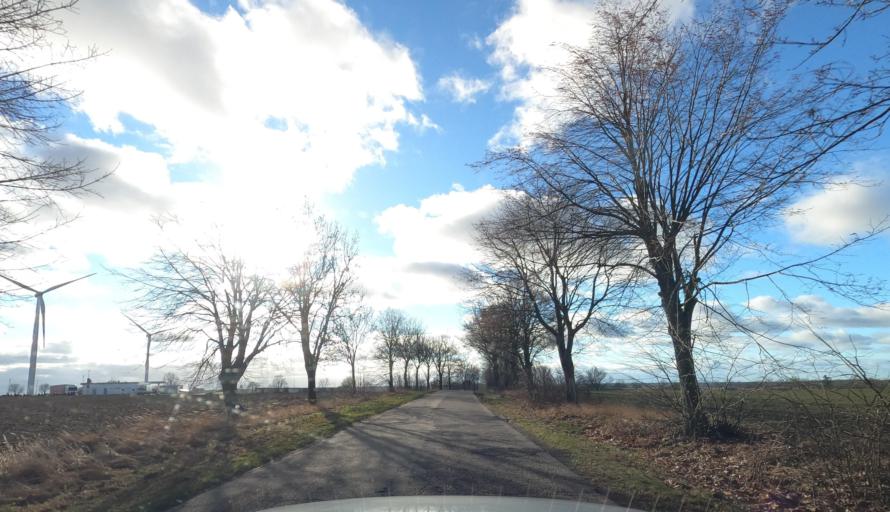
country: PL
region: West Pomeranian Voivodeship
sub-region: Powiat stargardzki
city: Suchan
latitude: 53.2925
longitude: 15.2349
